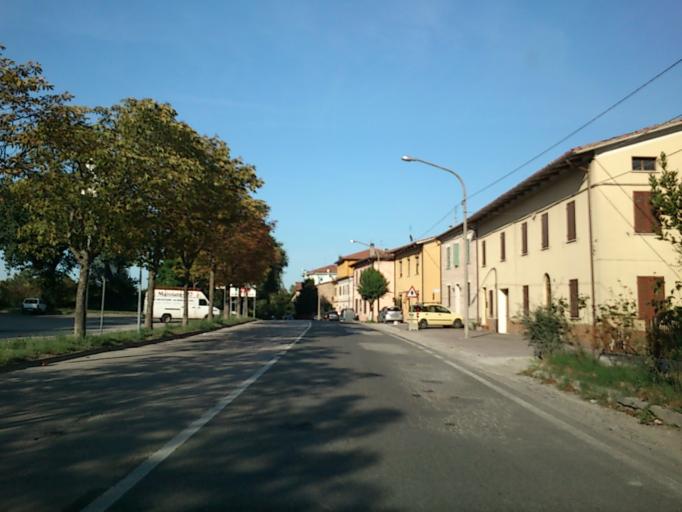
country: IT
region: The Marches
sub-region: Provincia di Pesaro e Urbino
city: Fossombrone
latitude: 43.6952
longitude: 12.8243
